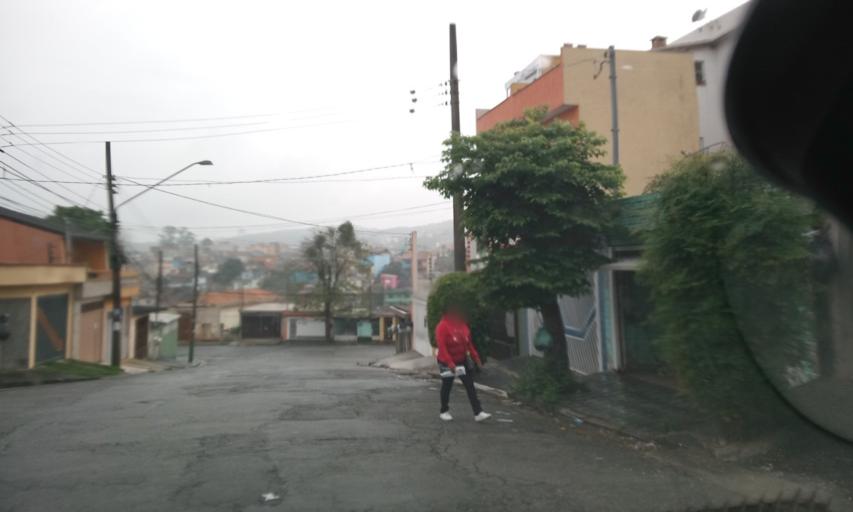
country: BR
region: Sao Paulo
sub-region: Santo Andre
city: Santo Andre
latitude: -23.7115
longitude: -46.5028
